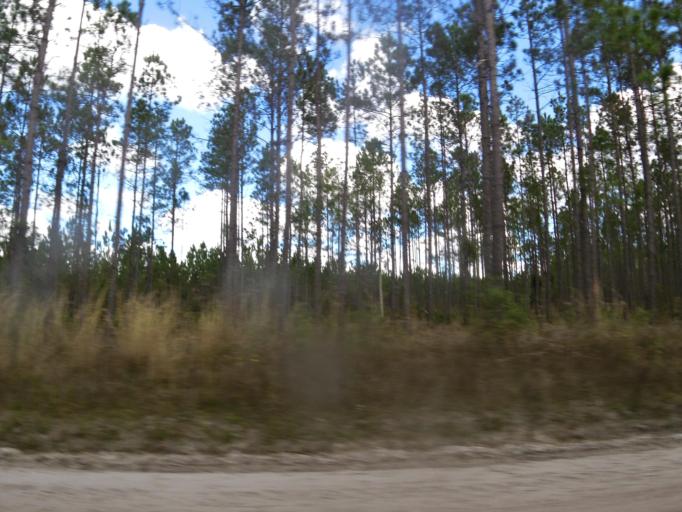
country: US
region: Florida
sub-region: Clay County
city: Green Cove Springs
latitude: 29.8370
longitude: -81.7590
